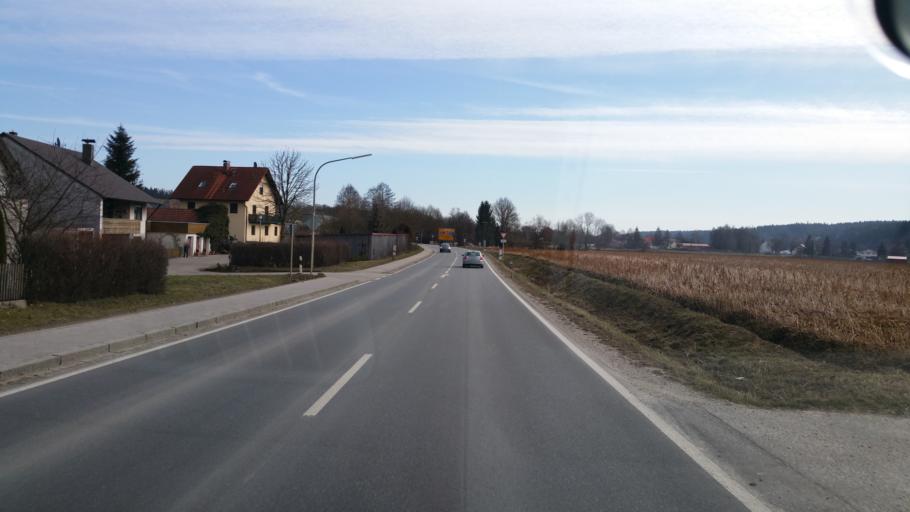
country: DE
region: Bavaria
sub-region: Lower Bavaria
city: Weihmichl
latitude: 48.5849
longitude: 12.0598
